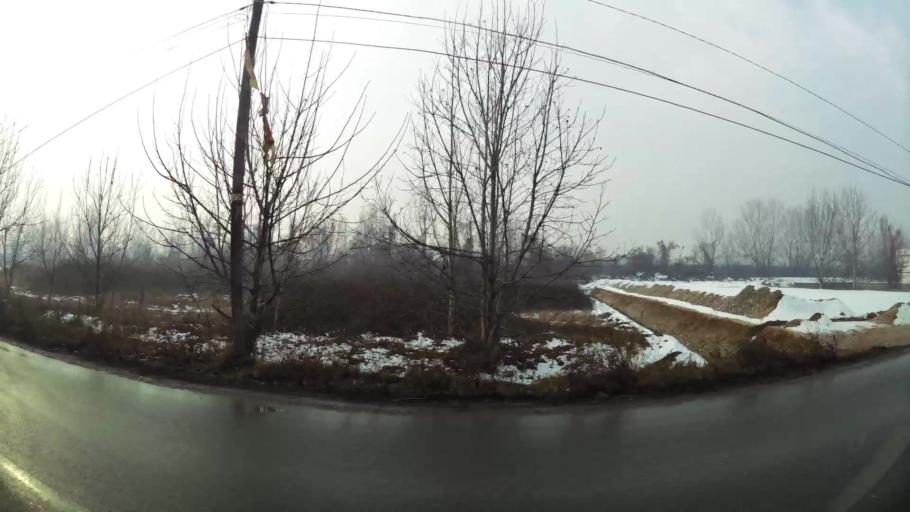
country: MK
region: Ilinden
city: Jurumleri
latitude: 41.9739
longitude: 21.5388
